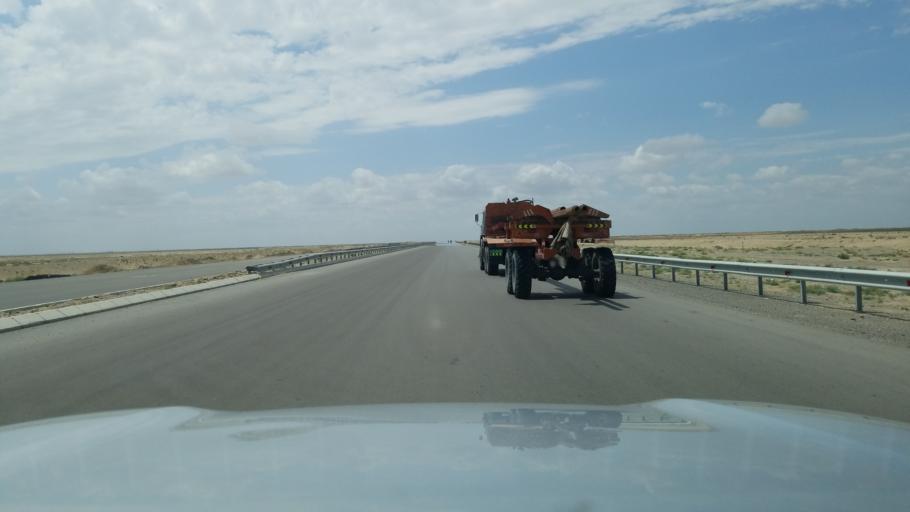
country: TM
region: Balkan
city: Gumdag
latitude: 39.2490
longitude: 54.6762
